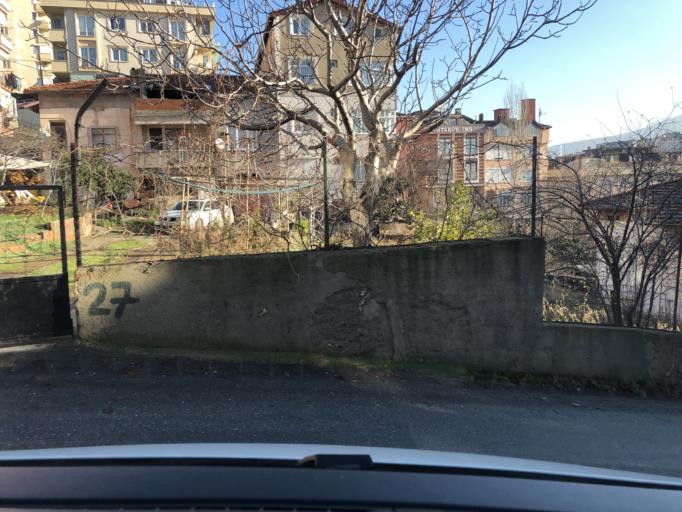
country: TR
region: Istanbul
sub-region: Atasehir
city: Atasehir
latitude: 40.9715
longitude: 29.1219
